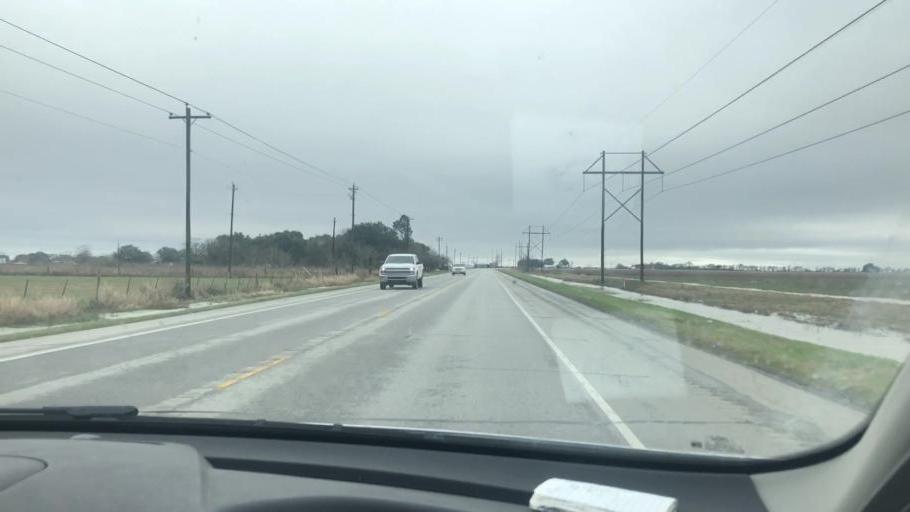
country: US
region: Texas
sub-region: Wharton County
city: Boling
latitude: 29.1493
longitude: -95.9893
